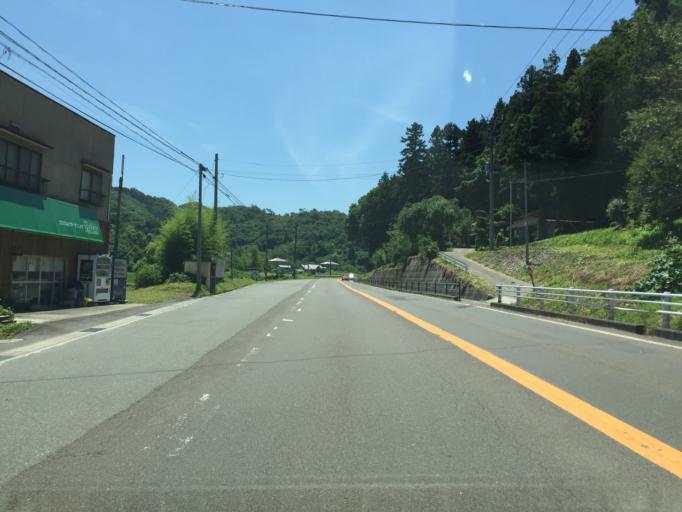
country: JP
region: Fukushima
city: Hobaramachi
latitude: 37.7618
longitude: 140.5643
